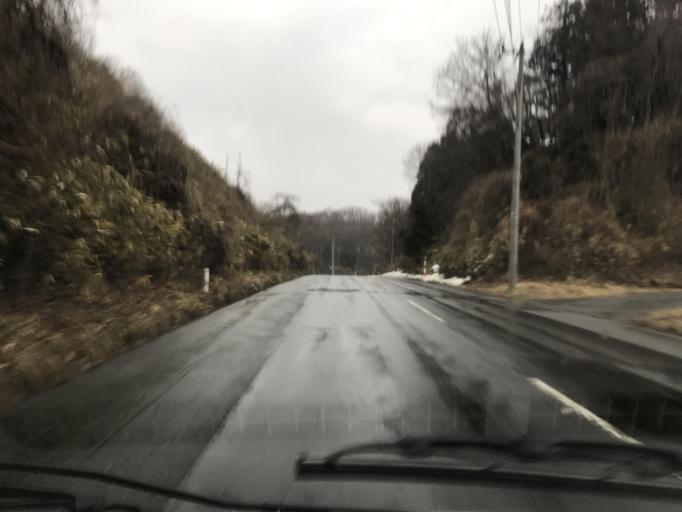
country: JP
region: Miyagi
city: Furukawa
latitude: 38.6831
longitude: 140.8715
